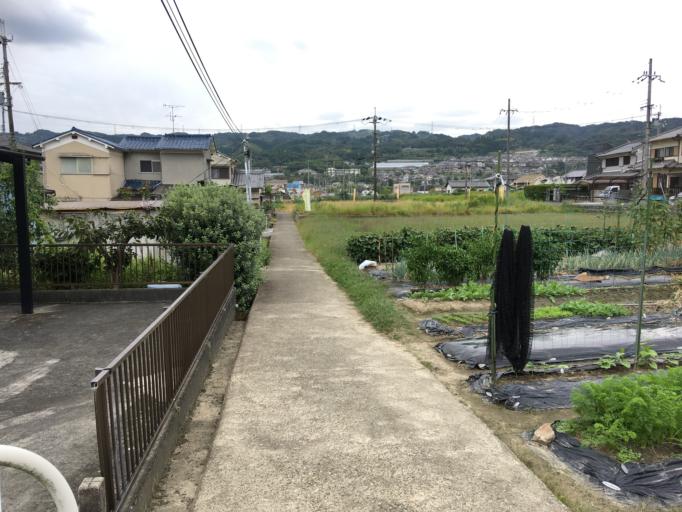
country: JP
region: Nara
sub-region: Ikoma-shi
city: Ikoma
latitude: 34.6320
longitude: 135.7044
